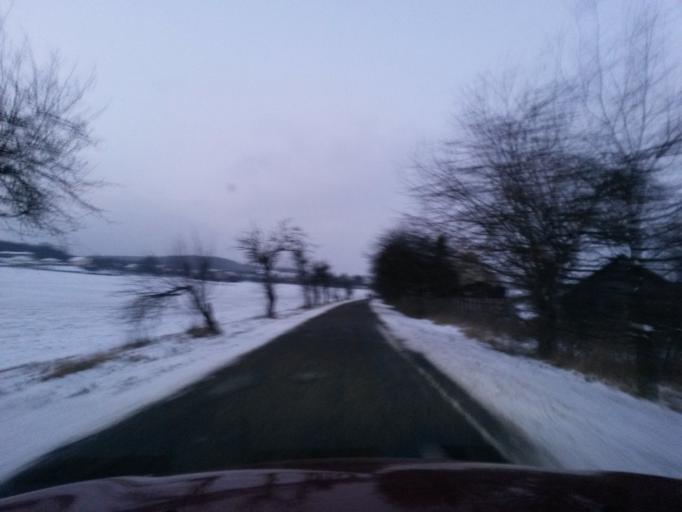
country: SK
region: Kosicky
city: Kosice
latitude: 48.7407
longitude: 21.3243
